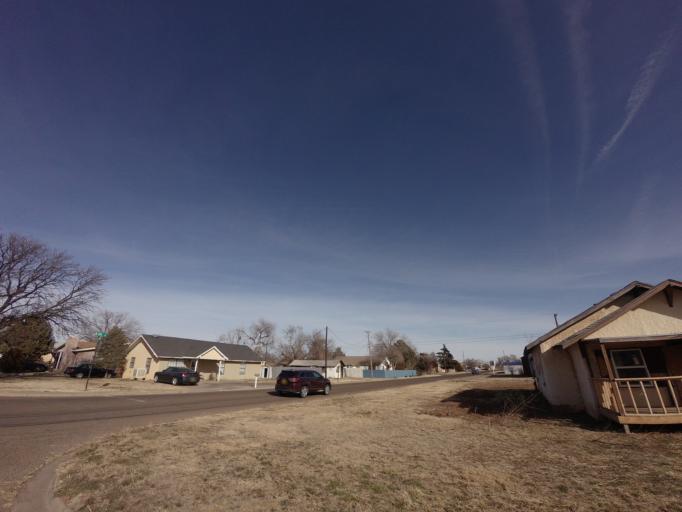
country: US
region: New Mexico
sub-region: Curry County
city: Clovis
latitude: 34.4056
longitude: -103.2179
